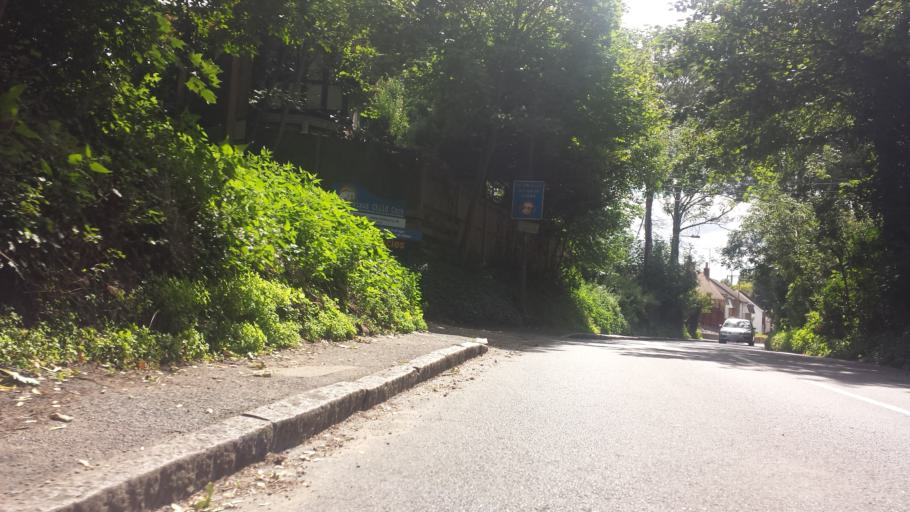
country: GB
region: England
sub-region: Greater London
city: Sidcup
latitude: 51.4039
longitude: 0.1196
